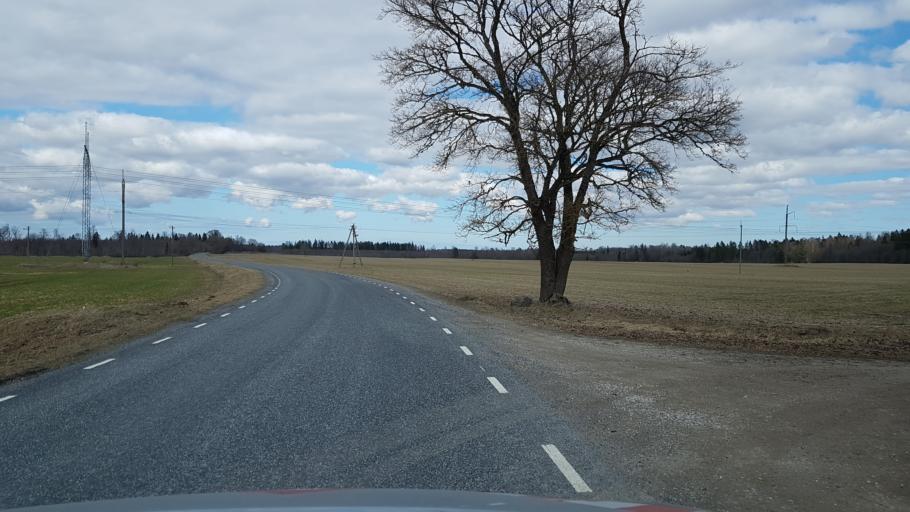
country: EE
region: Laeaene-Virumaa
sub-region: Tamsalu vald
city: Tamsalu
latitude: 59.1781
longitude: 26.1271
